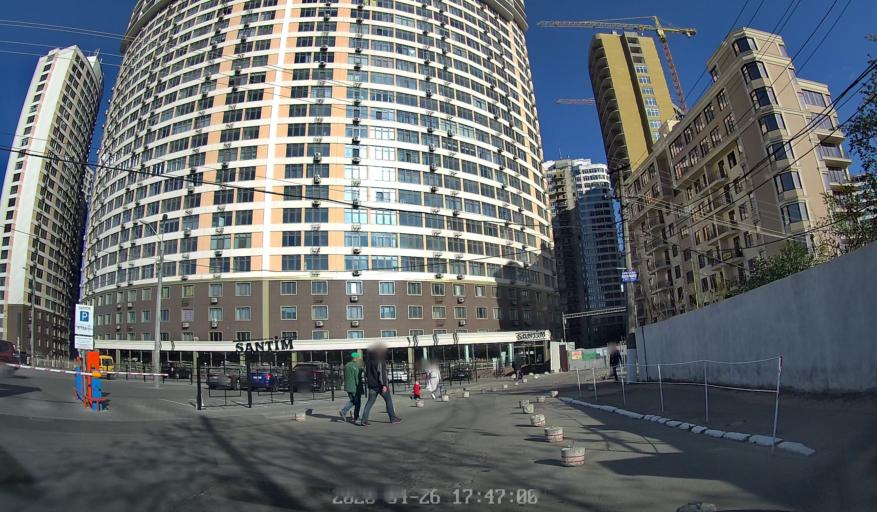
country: GR
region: South Aegean
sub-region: Nomos Kykladon
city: Serifos
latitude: 37.1388
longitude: 24.6077
